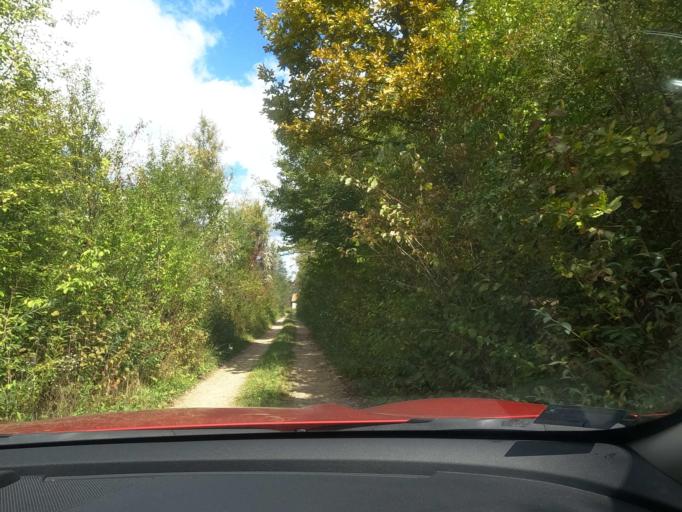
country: BA
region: Federation of Bosnia and Herzegovina
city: Velika Kladusa
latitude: 45.2339
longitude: 15.7746
